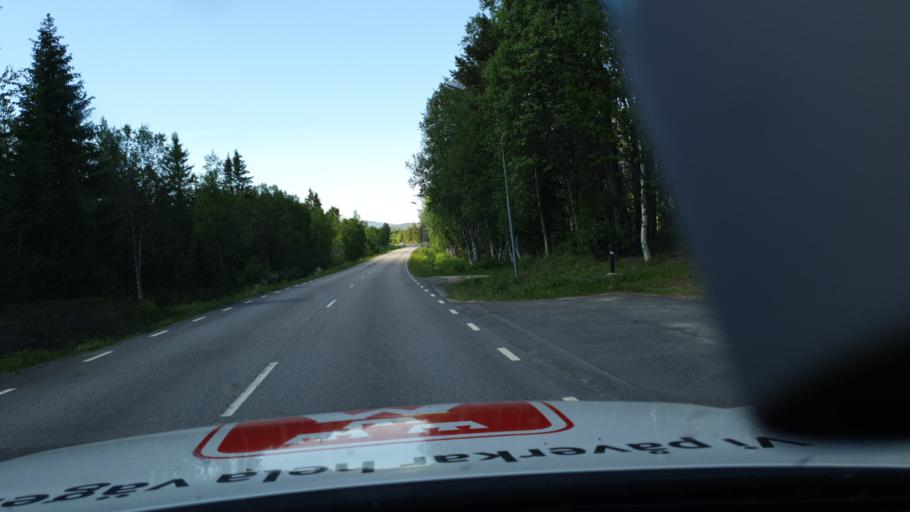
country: SE
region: Jaemtland
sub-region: Harjedalens Kommun
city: Sveg
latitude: 62.1038
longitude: 13.4928
